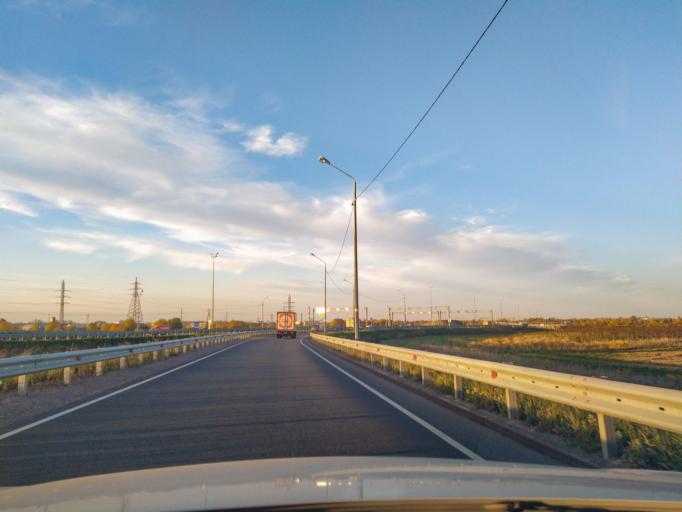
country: RU
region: Leningrad
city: Gatchina
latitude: 59.5354
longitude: 30.1573
